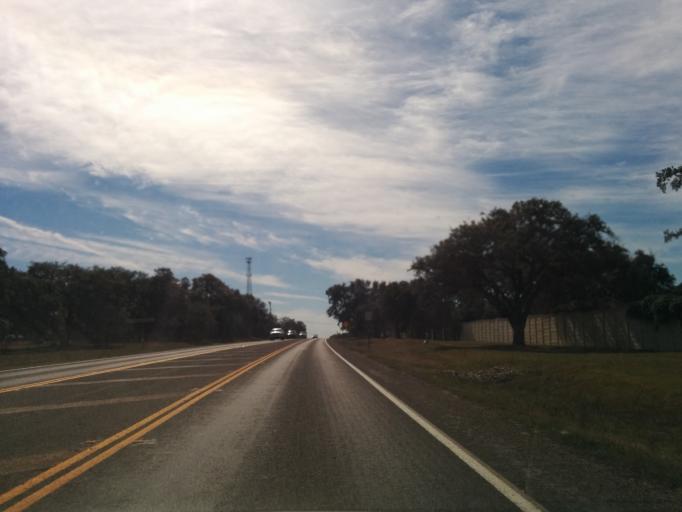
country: US
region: Texas
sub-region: Bexar County
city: Fair Oaks Ranch
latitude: 29.7379
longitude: -98.6234
